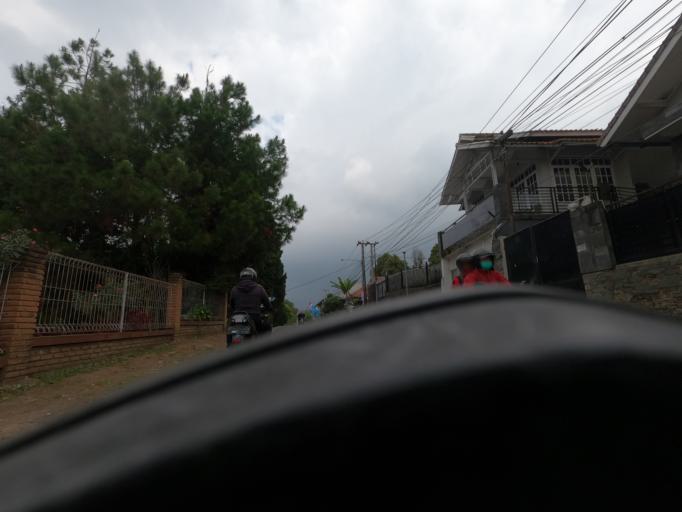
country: ID
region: West Java
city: Cimahi
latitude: -6.8160
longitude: 107.5516
